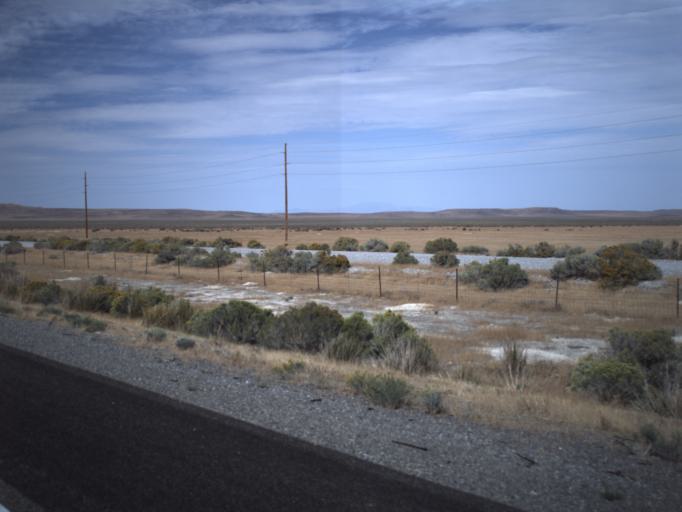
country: US
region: Utah
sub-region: Tooele County
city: Grantsville
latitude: 40.7526
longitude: -113.0406
